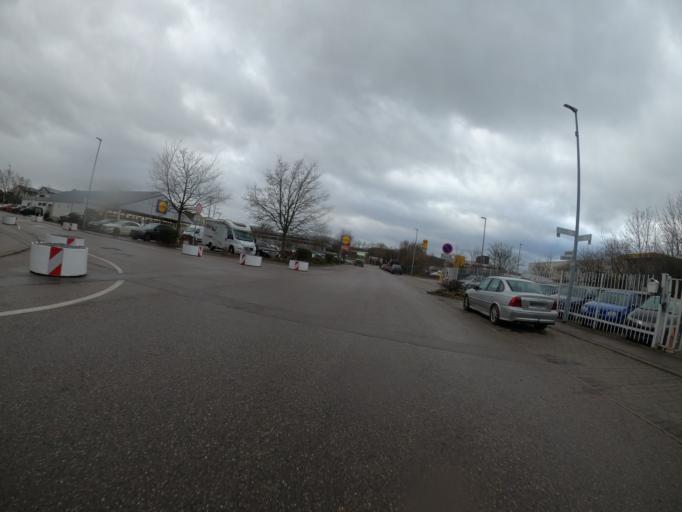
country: DE
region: Baden-Wuerttemberg
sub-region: Regierungsbezirk Stuttgart
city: Salach
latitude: 48.6895
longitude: 9.7282
